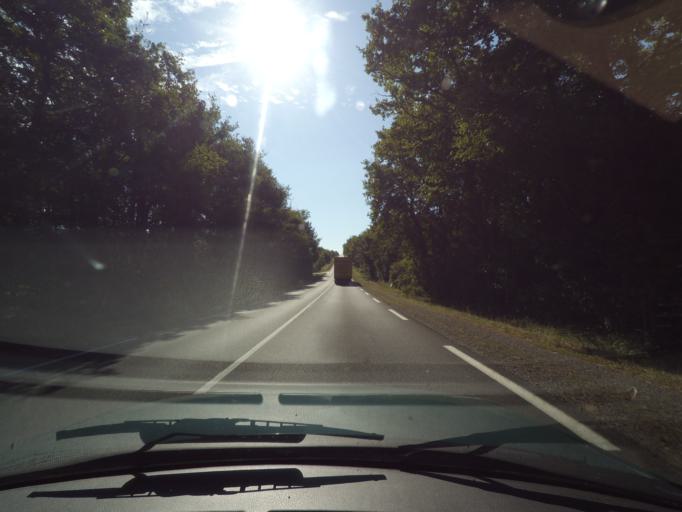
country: FR
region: Poitou-Charentes
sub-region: Departement de la Vienne
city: Terce
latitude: 46.4284
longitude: 0.6171
